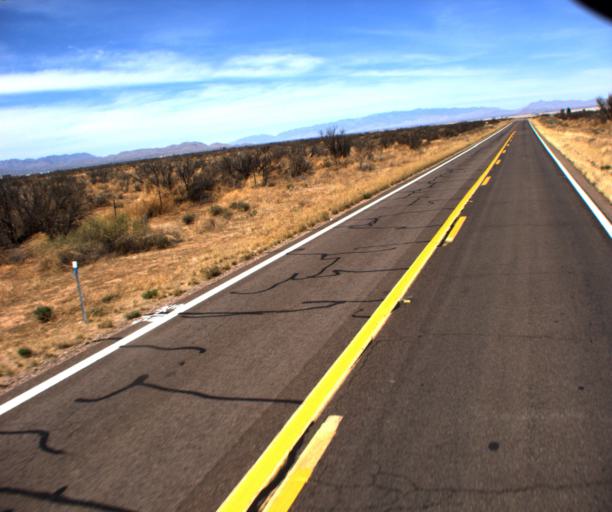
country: US
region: Arizona
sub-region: Cochise County
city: Willcox
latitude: 32.1103
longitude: -109.9135
